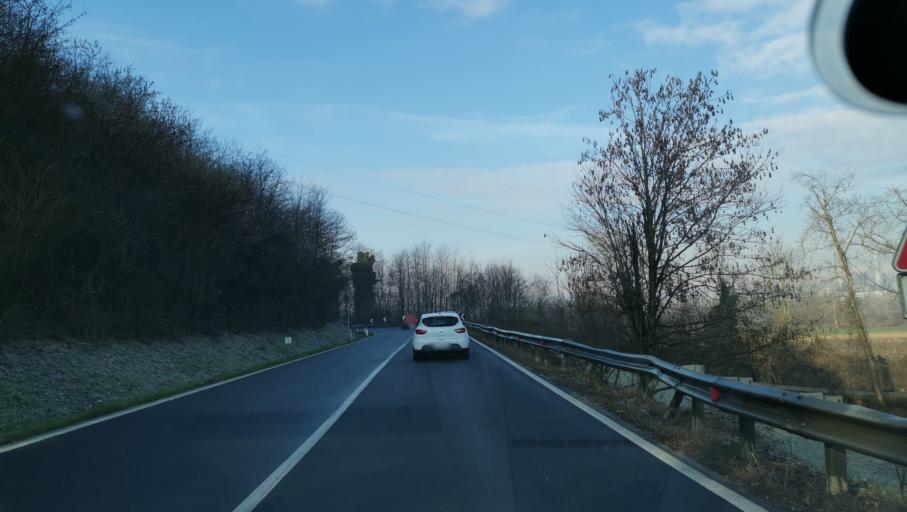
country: IT
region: Piedmont
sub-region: Provincia di Torino
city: Chivasso
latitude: 45.1772
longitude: 7.9091
